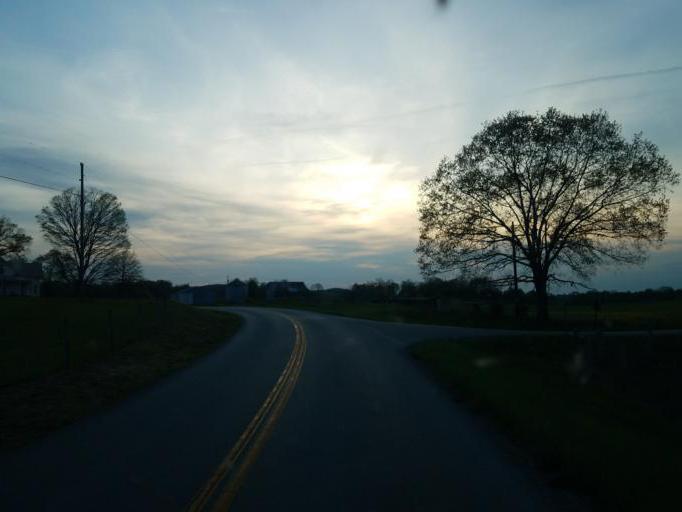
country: US
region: Kentucky
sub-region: Hart County
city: Munfordville
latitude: 37.2419
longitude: -85.7334
